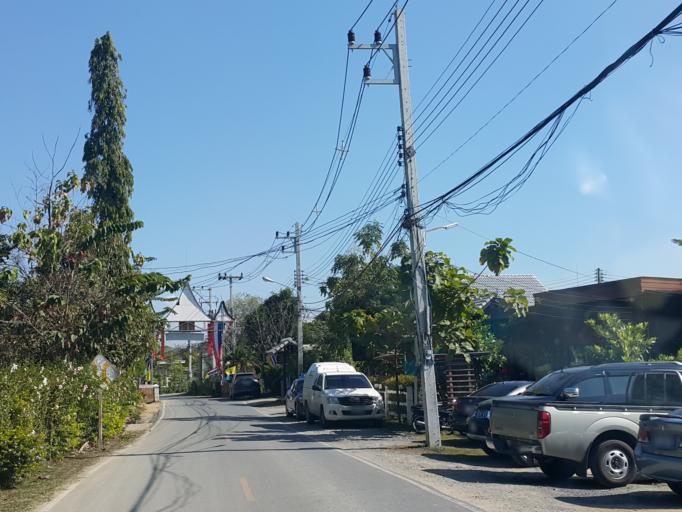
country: TH
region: Chiang Mai
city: San Sai
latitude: 18.8751
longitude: 99.0077
